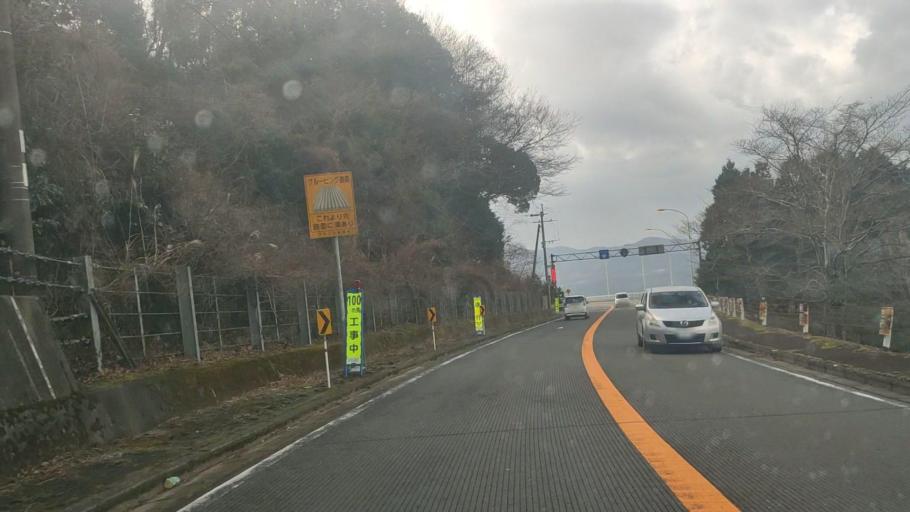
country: JP
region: Kumamoto
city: Hitoyoshi
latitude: 32.0818
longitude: 130.8002
